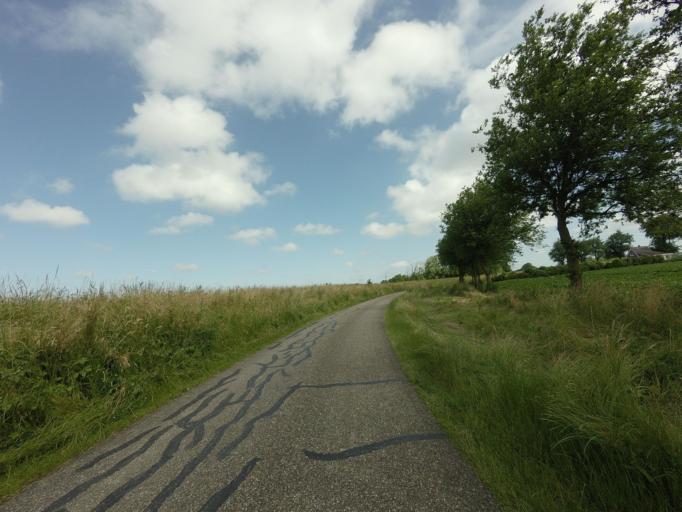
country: NL
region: North Holland
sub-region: Gemeente Schagen
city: Schagen
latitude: 52.8410
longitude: 4.8087
